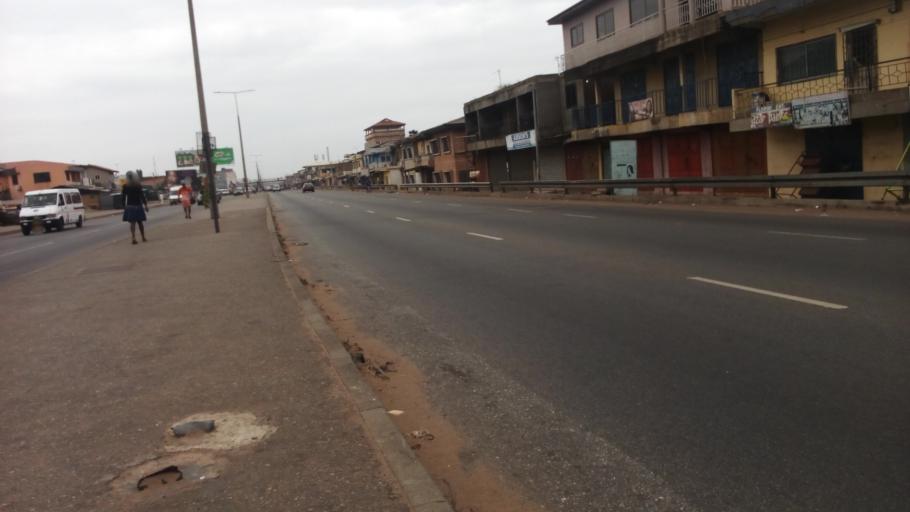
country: GH
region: Greater Accra
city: Accra
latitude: 5.5684
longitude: -0.2411
